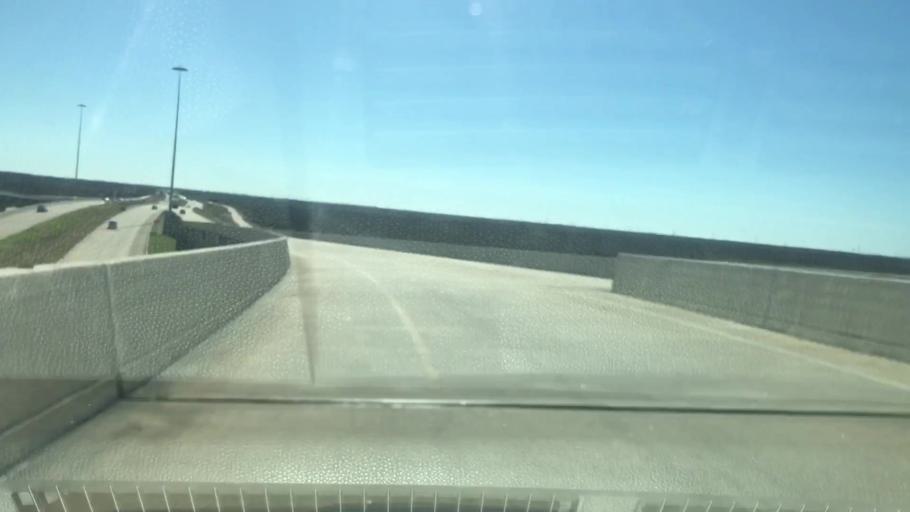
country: US
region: Texas
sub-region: Harris County
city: Cypress
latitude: 29.9962
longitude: -95.7691
